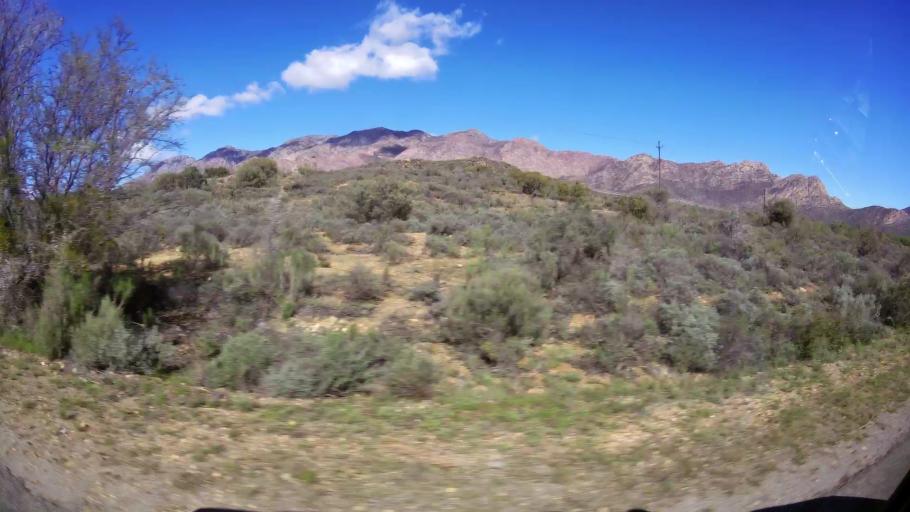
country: ZA
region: Western Cape
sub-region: Cape Winelands District Municipality
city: Ashton
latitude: -33.7889
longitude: 20.1341
